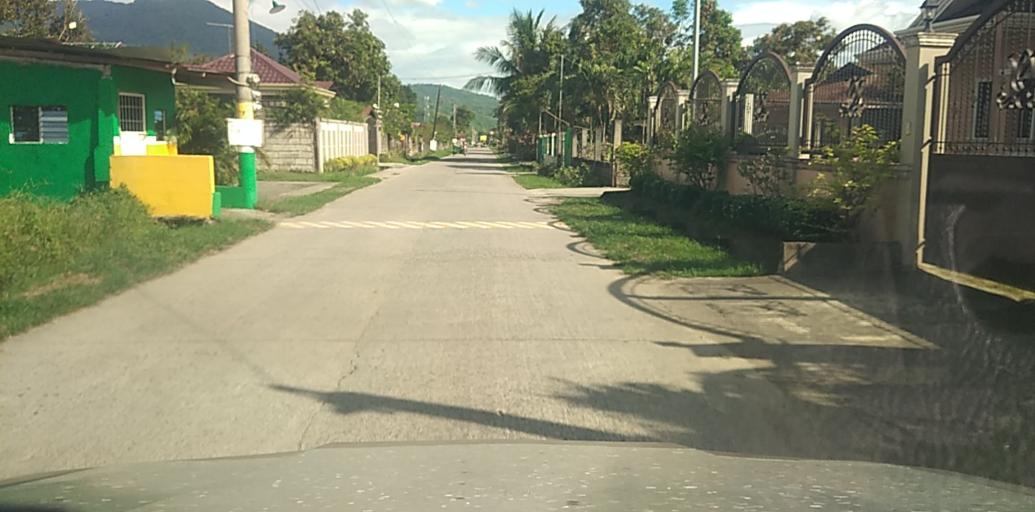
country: PH
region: Central Luzon
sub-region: Province of Pampanga
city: Buensuseso
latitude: 15.1929
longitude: 120.6827
